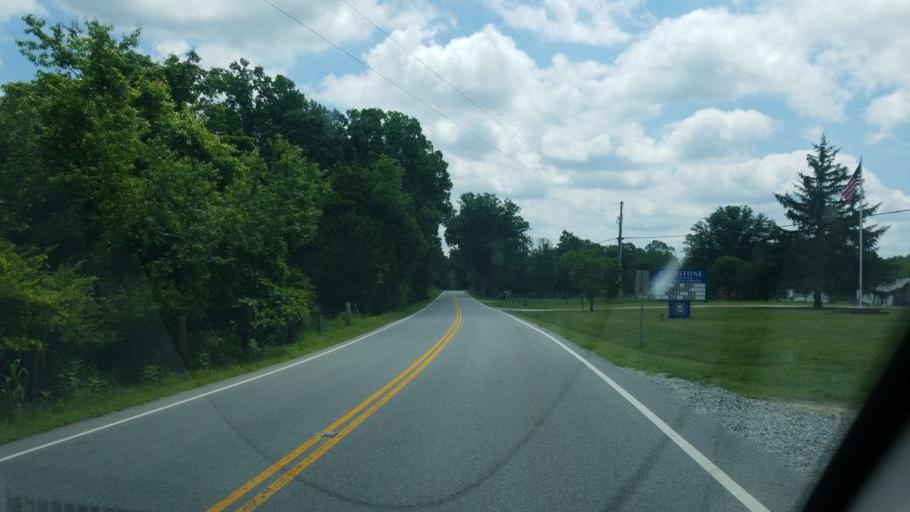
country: US
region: Virginia
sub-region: Appomattox County
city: Appomattox
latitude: 37.5508
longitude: -78.8363
